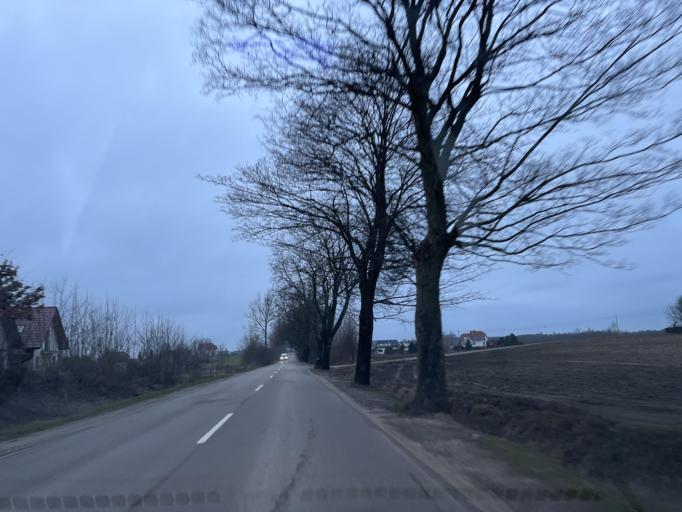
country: PL
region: Pomeranian Voivodeship
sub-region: Powiat kartuski
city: Kartuzy
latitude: 54.4052
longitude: 18.2161
